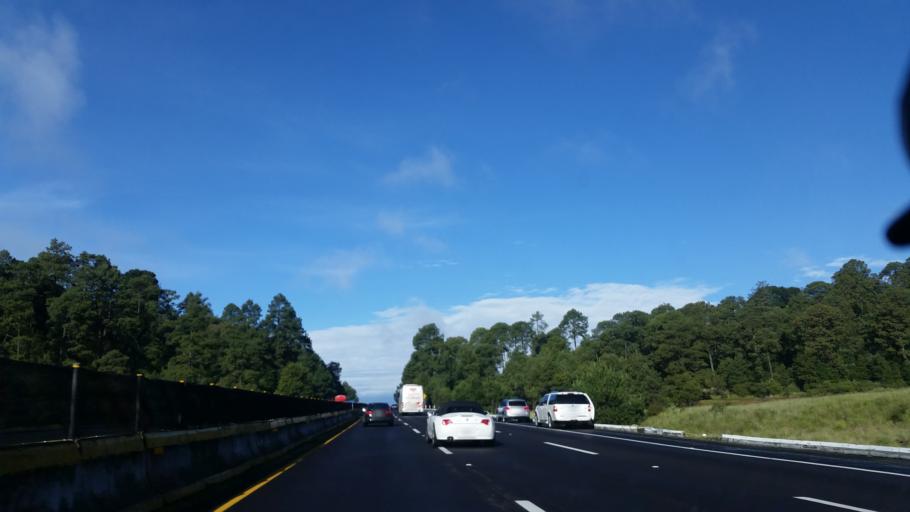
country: MX
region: Morelos
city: Tres Marias
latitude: 19.1024
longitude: -99.1981
